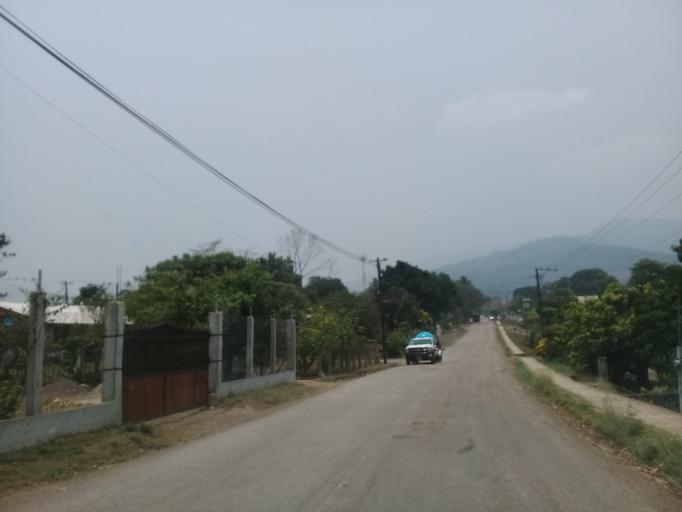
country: MX
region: Veracruz
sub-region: Tezonapa
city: Laguna Chica (Pueblo Nuevo)
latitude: 18.5397
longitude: -96.7328
